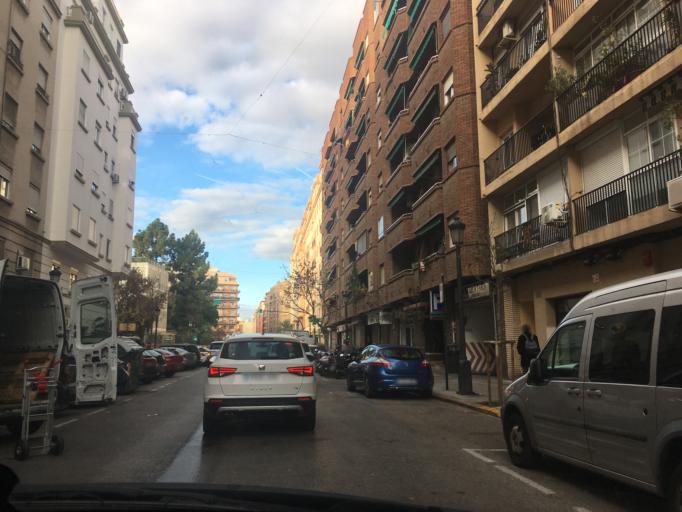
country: ES
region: Valencia
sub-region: Provincia de Valencia
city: Valencia
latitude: 39.4745
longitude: -0.3927
